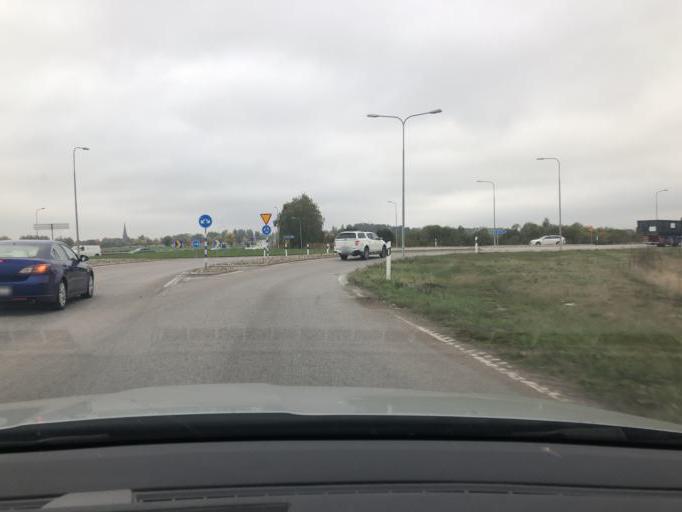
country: SE
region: Uppsala
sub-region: Uppsala Kommun
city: Gamla Uppsala
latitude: 59.8878
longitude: 17.6948
